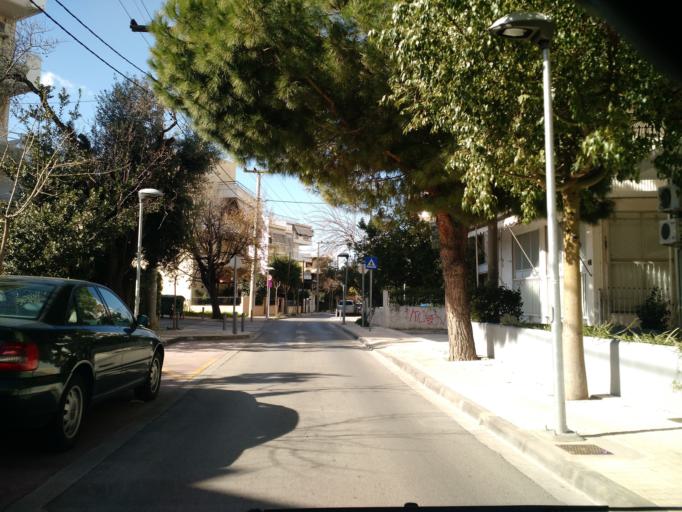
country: GR
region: Attica
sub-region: Nomarchia Athinas
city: Agia Paraskevi
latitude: 38.0200
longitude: 23.8227
